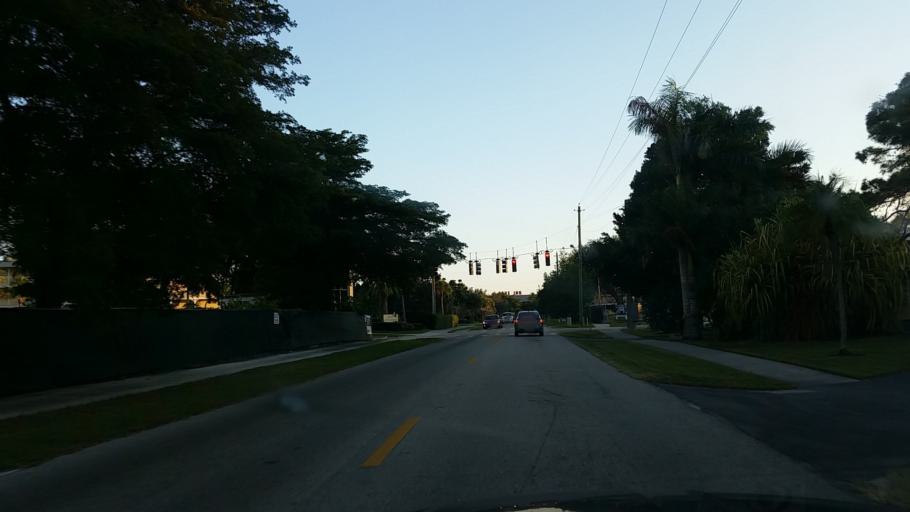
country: US
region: Florida
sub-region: Collier County
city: Naples
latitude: 26.1371
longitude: -81.7941
